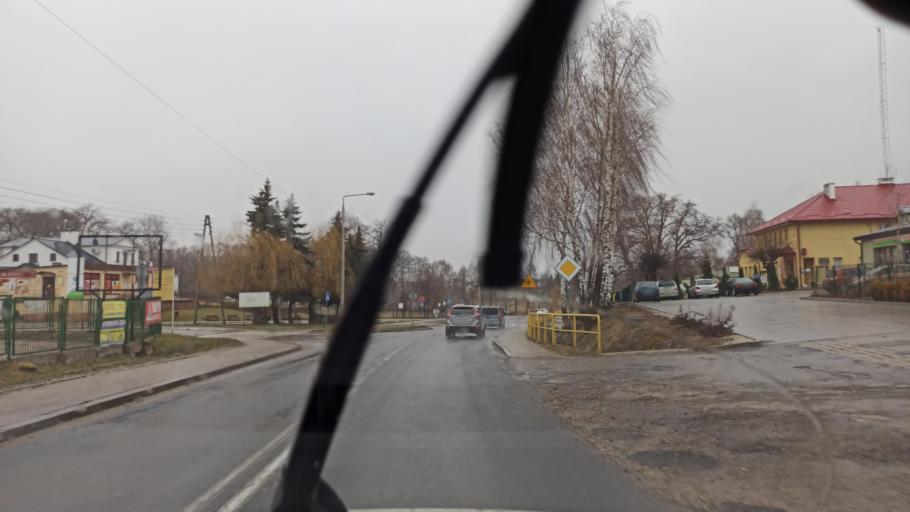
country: PL
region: Lublin Voivodeship
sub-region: Powiat lubelski
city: Strzyzowice
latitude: 51.0496
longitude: 22.4487
